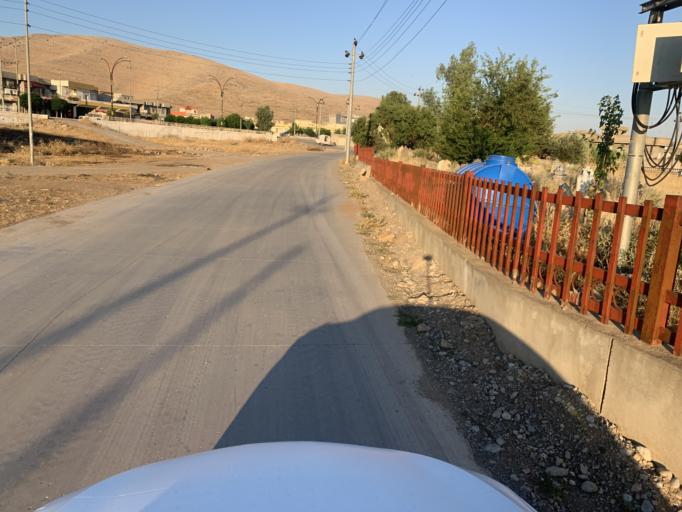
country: IQ
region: As Sulaymaniyah
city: Raniye
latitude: 36.2715
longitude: 44.7590
